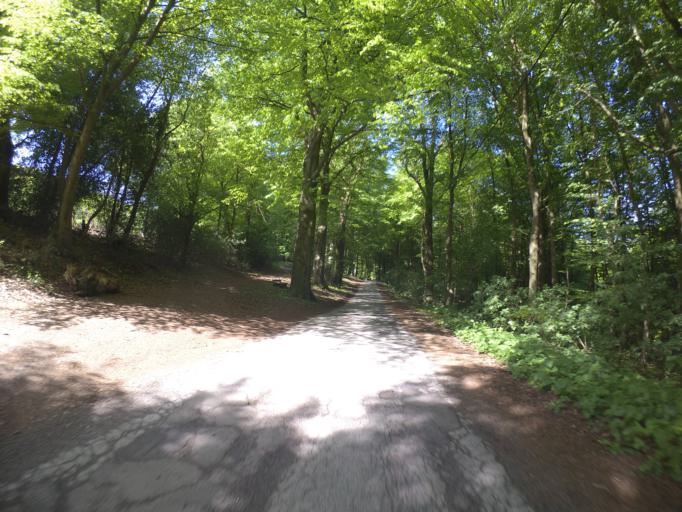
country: DE
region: North Rhine-Westphalia
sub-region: Regierungsbezirk Arnsberg
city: Schwelm
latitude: 51.2703
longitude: 7.2717
